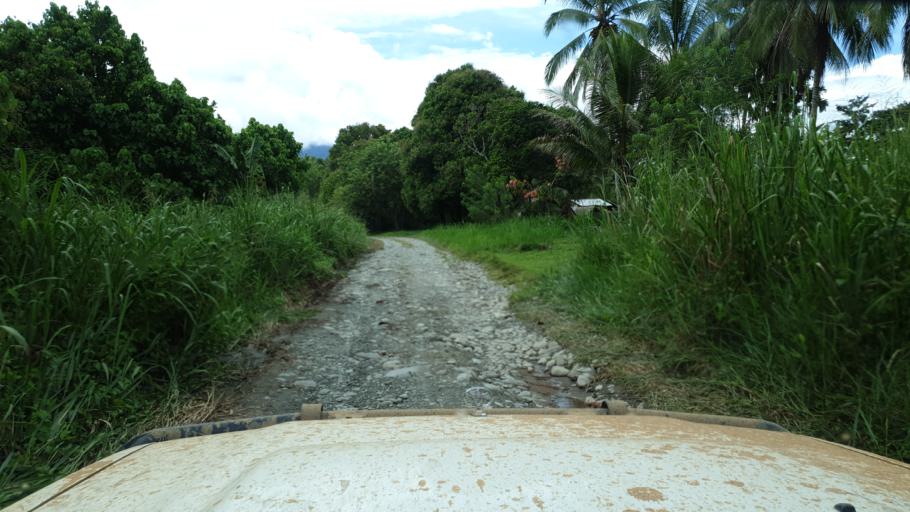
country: PG
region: Northern Province
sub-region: Sohe
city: Kokoda
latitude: -8.9189
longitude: 147.8758
